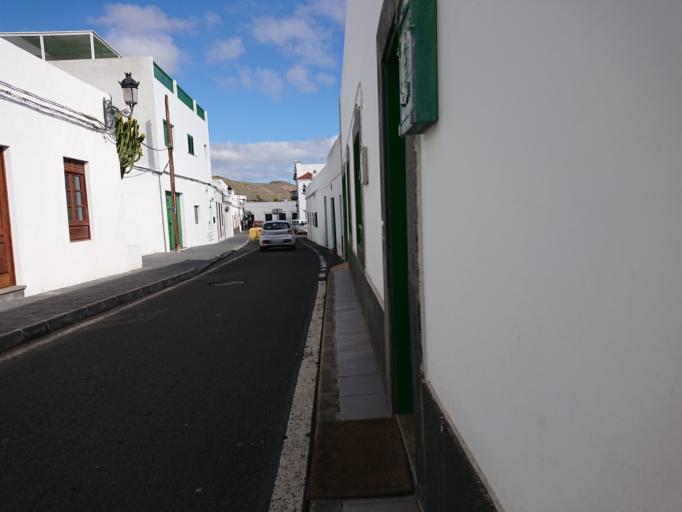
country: ES
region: Canary Islands
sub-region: Provincia de Las Palmas
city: Haria
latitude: 29.1458
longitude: -13.5010
